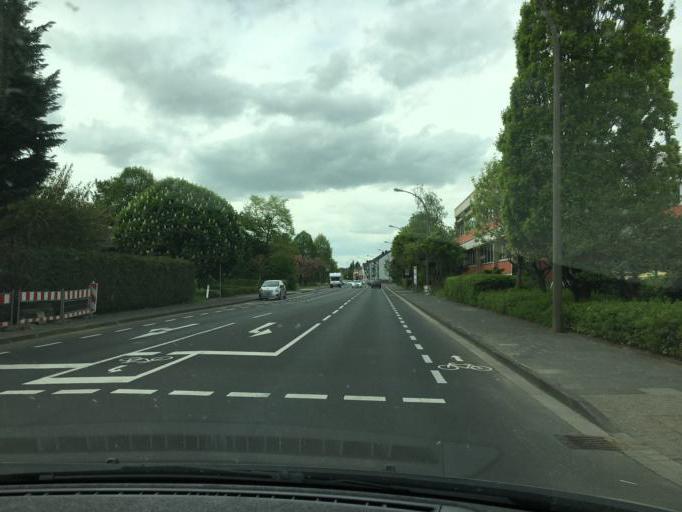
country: DE
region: North Rhine-Westphalia
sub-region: Regierungsbezirk Koln
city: Euskirchen
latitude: 50.6660
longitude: 6.7956
